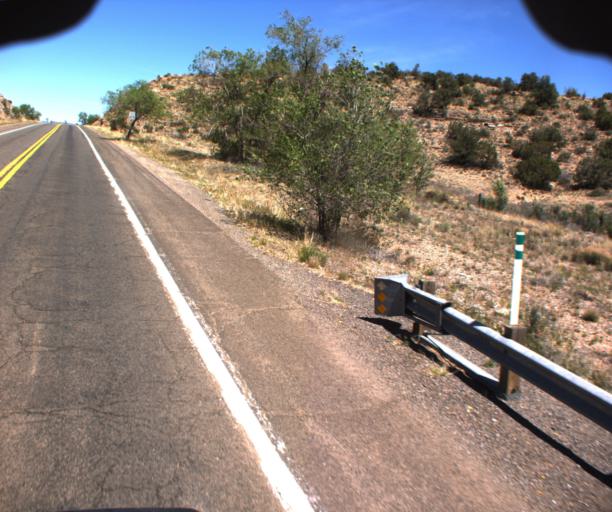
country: US
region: Arizona
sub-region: Mohave County
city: Peach Springs
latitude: 35.5318
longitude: -113.4207
